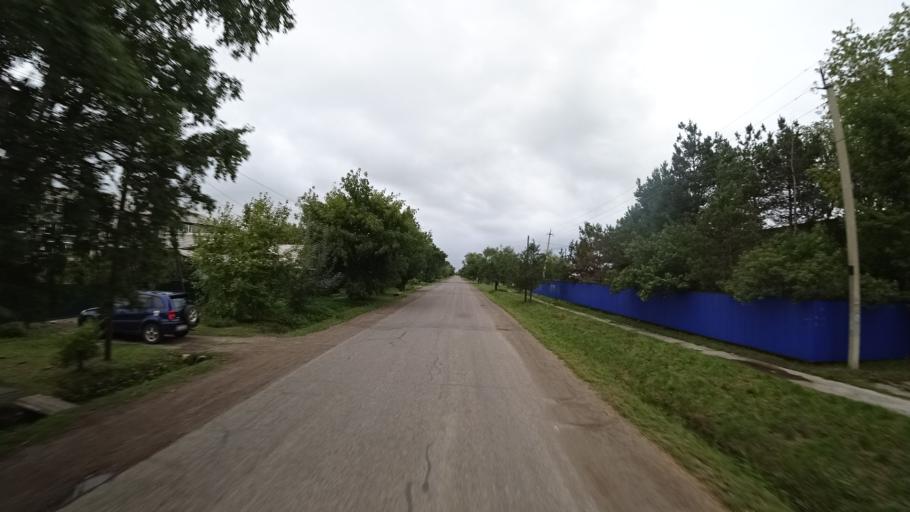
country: RU
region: Primorskiy
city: Chernigovka
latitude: 44.3402
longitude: 132.5846
